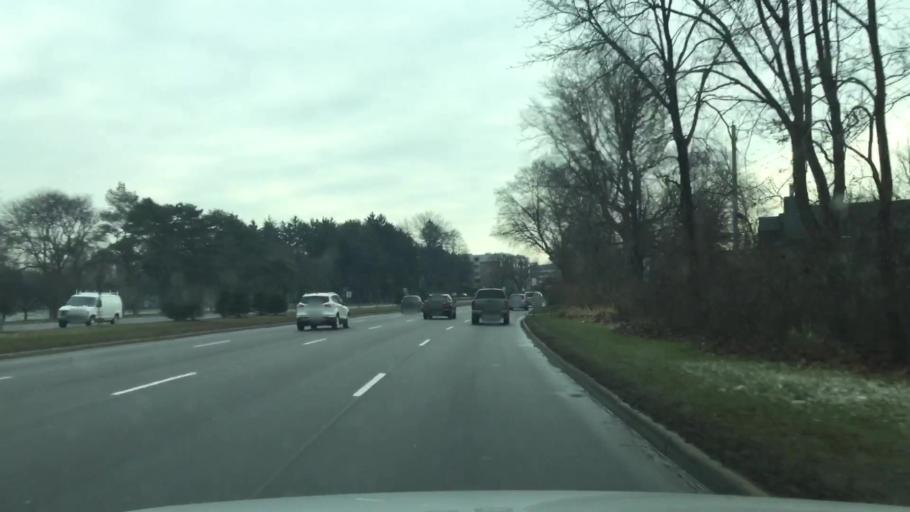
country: US
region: Michigan
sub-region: Oakland County
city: Birmingham
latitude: 42.5521
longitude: -83.2157
